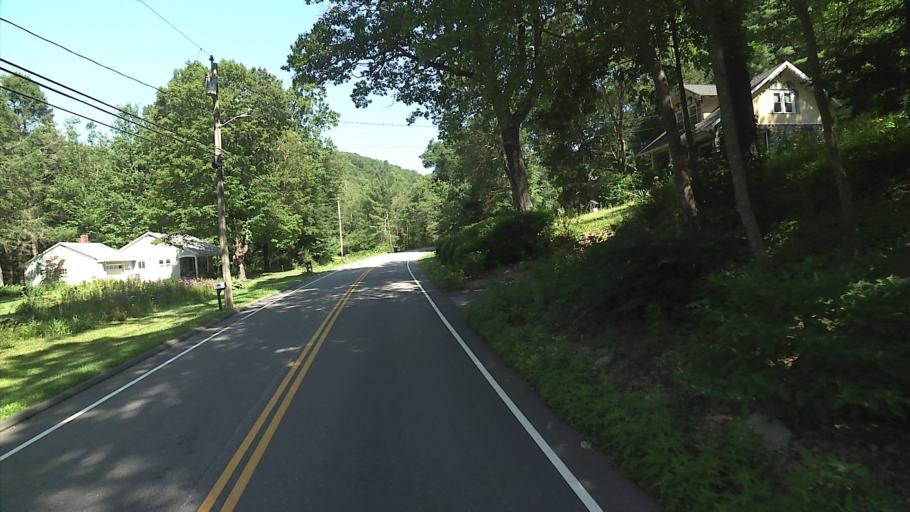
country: US
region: Connecticut
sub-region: Litchfield County
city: West Torrington
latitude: 41.8298
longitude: -73.1508
